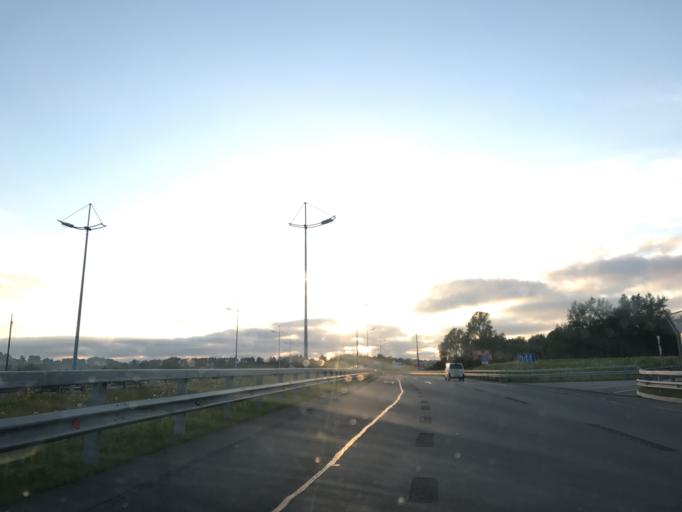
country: RU
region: Kaliningrad
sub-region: Gorod Svetlogorsk
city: Svetlogorsk
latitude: 54.9171
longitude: 20.1916
